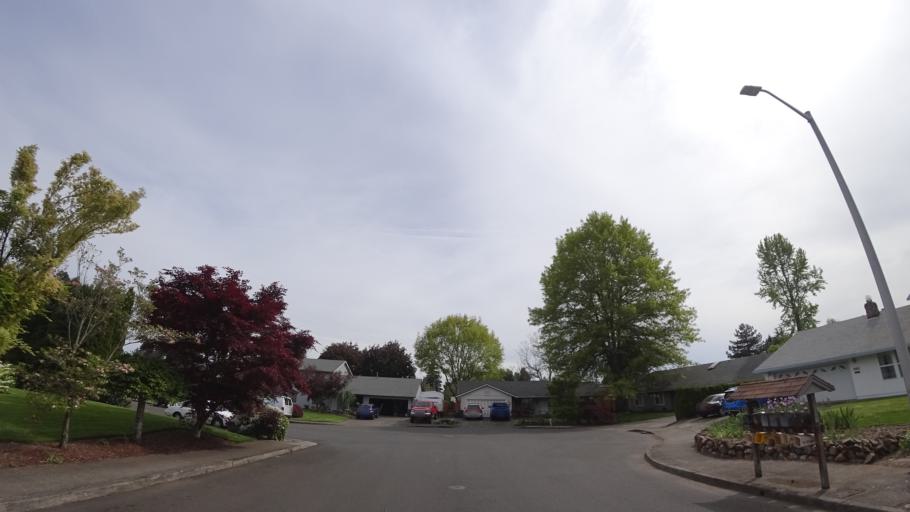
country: US
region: Oregon
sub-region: Washington County
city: Hillsboro
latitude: 45.5171
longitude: -122.9487
